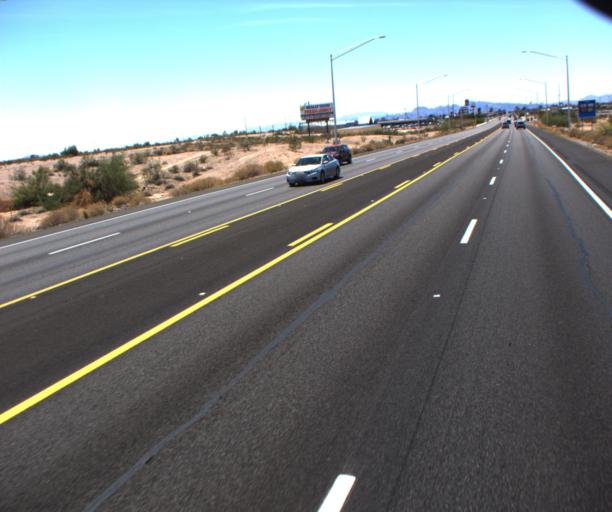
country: US
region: Arizona
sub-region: La Paz County
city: Parker
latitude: 34.1581
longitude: -114.2713
